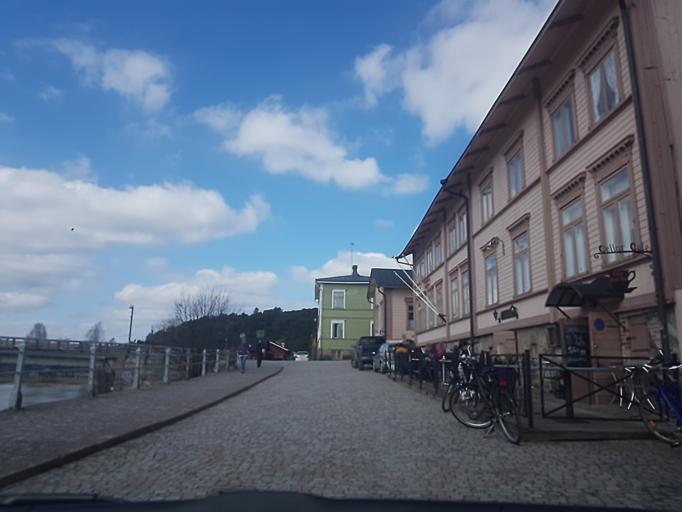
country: FI
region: Uusimaa
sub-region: Porvoo
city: Porvoo
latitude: 60.3965
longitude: 25.6562
